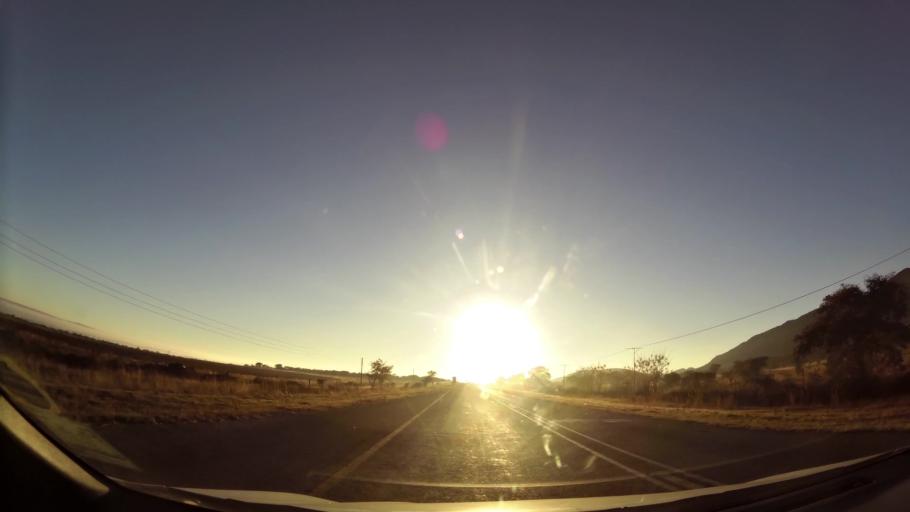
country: ZA
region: Limpopo
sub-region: Capricorn District Municipality
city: Polokwane
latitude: -24.0175
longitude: 29.3120
